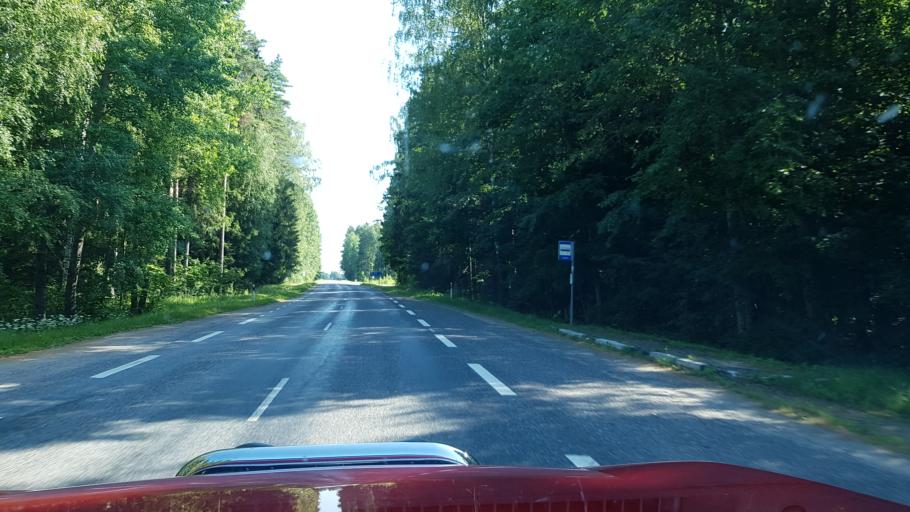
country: EE
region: Polvamaa
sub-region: Polva linn
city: Polva
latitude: 57.9929
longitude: 26.9052
